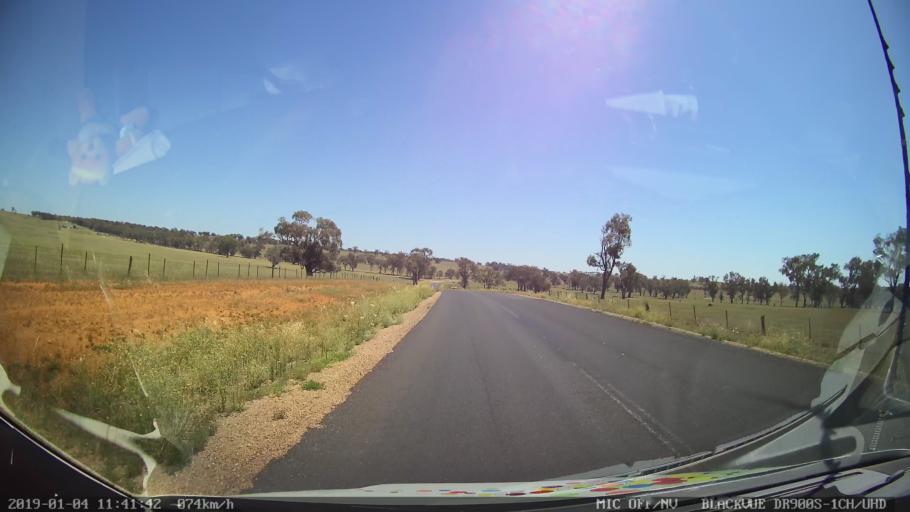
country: AU
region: New South Wales
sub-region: Cabonne
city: Molong
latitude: -32.9907
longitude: 148.7874
